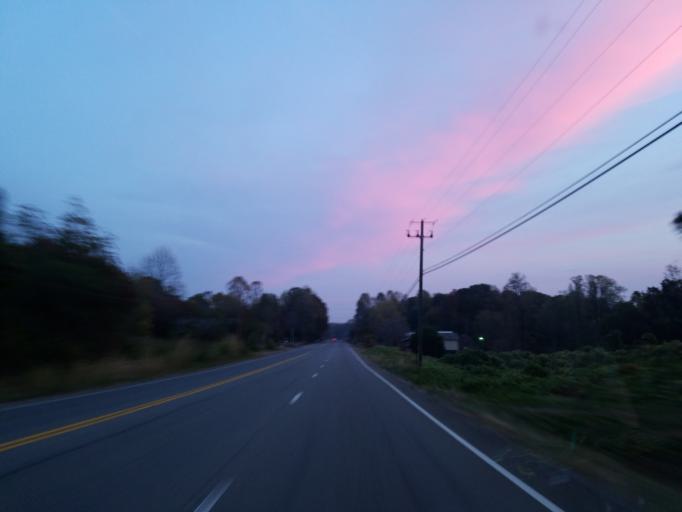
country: US
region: Georgia
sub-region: Pickens County
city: Jasper
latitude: 34.4890
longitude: -84.4599
